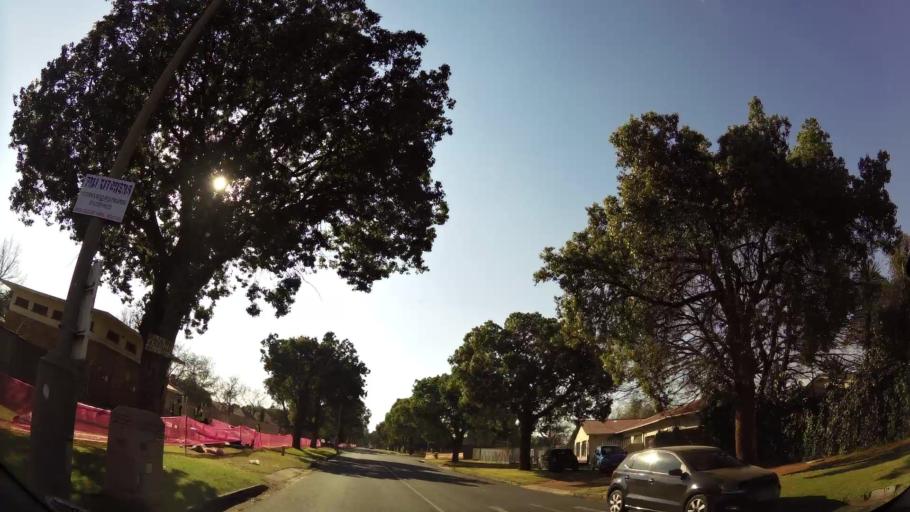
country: ZA
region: Gauteng
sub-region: Ekurhuleni Metropolitan Municipality
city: Benoni
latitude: -26.1560
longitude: 28.3037
